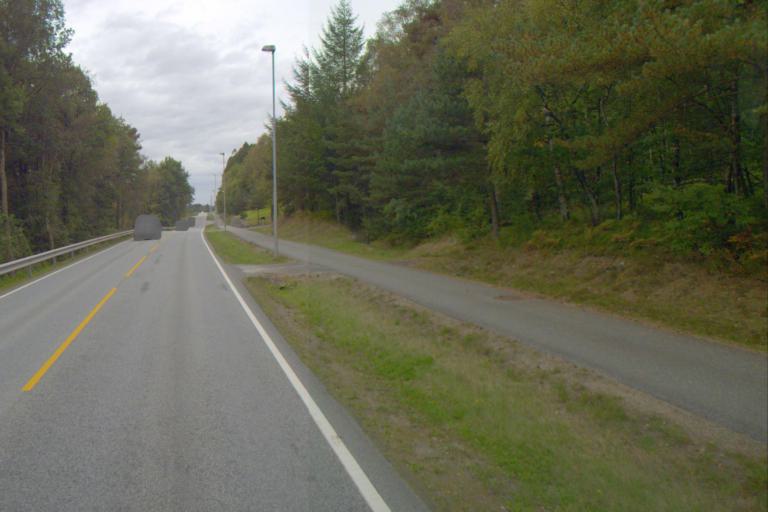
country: NO
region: Rogaland
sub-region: Sandnes
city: Hommersak
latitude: 58.8791
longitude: 5.8300
